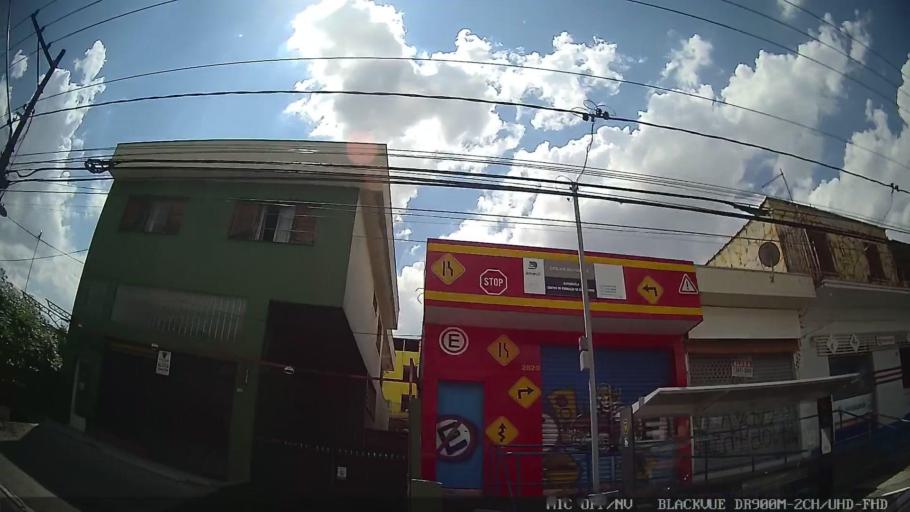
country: BR
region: Sao Paulo
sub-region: Ferraz De Vasconcelos
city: Ferraz de Vasconcelos
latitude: -23.5553
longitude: -46.4682
